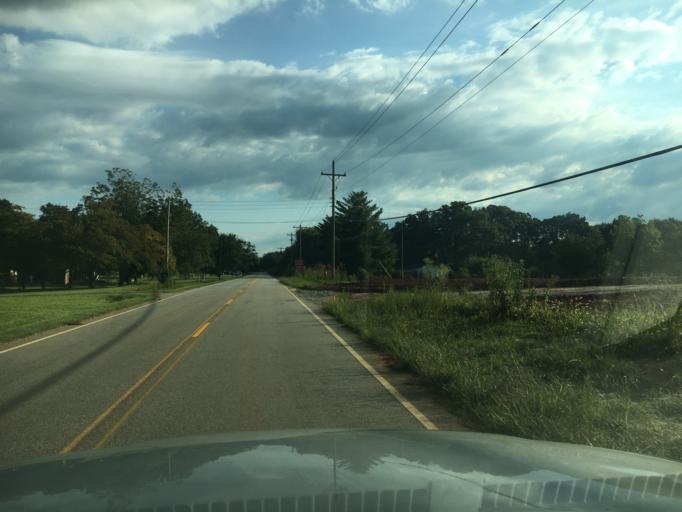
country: US
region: South Carolina
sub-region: Spartanburg County
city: Wellford
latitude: 34.9190
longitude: -82.1074
